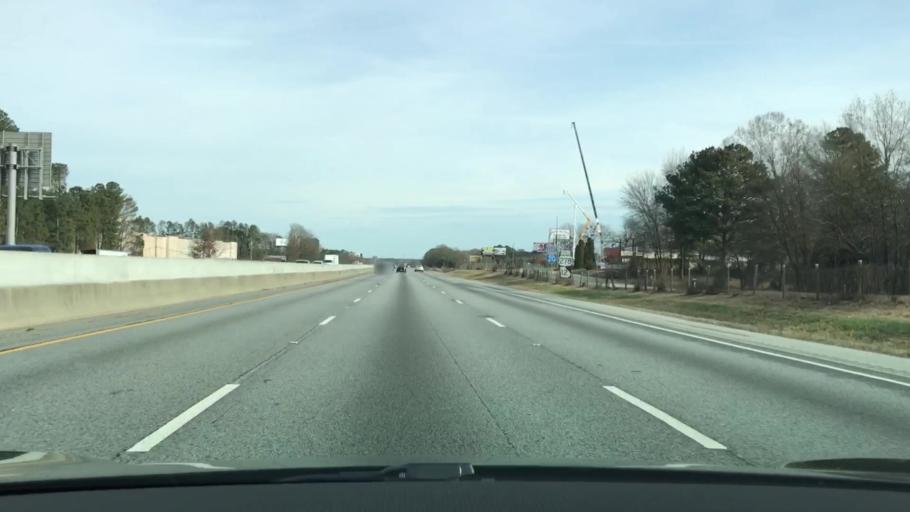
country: US
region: Georgia
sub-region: Rockdale County
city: Conyers
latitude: 33.6312
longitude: -83.9680
